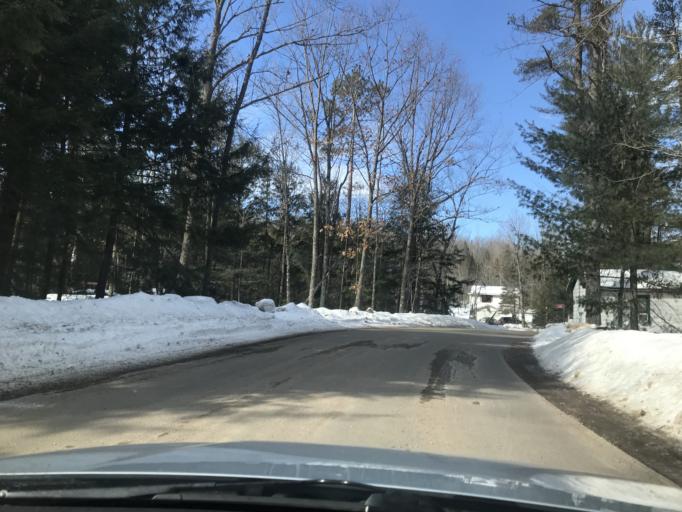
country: US
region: Wisconsin
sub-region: Oconto County
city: Gillett
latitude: 45.1254
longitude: -88.4206
